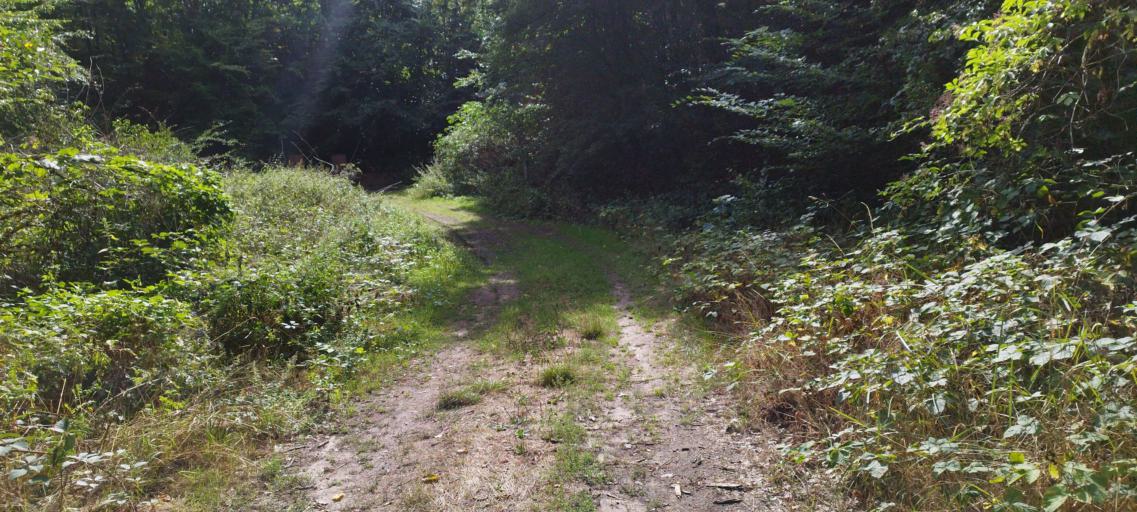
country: DE
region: Brandenburg
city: Wiesenburg
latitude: 52.1073
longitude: 12.4996
